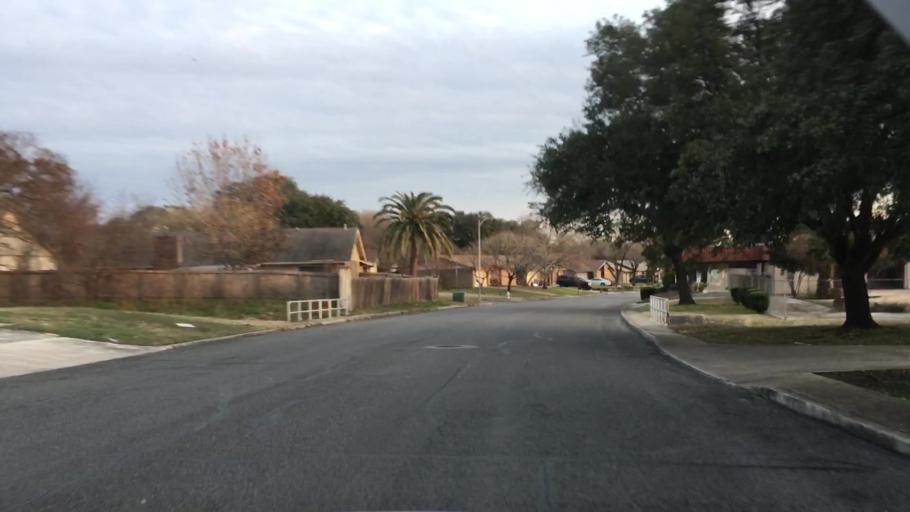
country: US
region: Texas
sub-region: Bexar County
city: Windcrest
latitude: 29.5598
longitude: -98.3941
